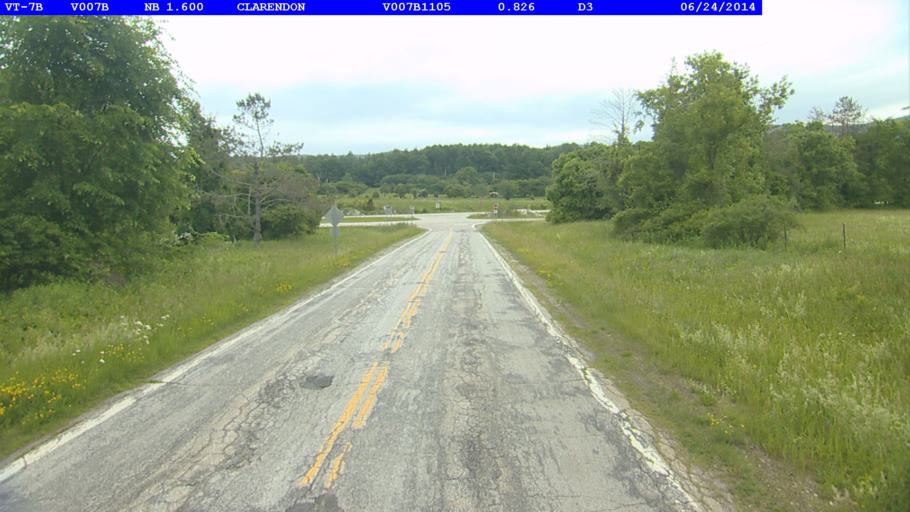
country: US
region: Vermont
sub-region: Rutland County
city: Rutland
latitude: 43.5059
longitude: -72.9686
